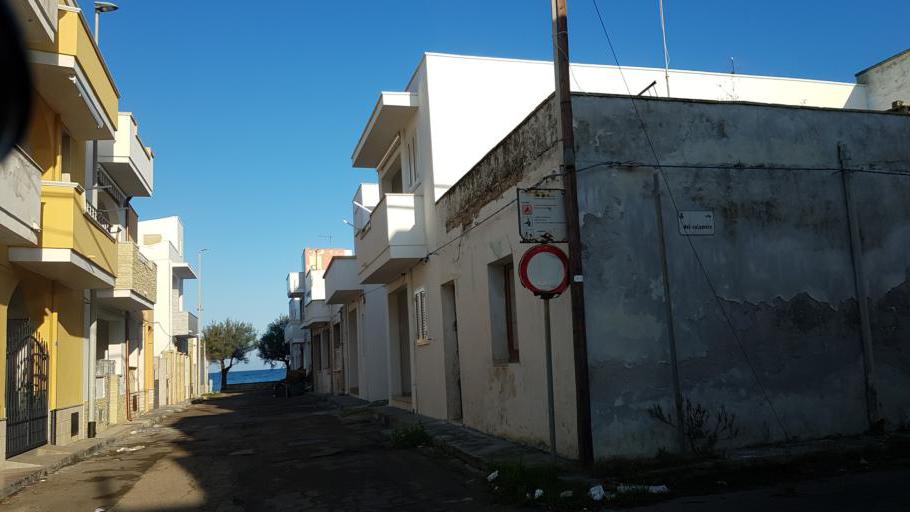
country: IT
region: Apulia
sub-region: Provincia di Brindisi
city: Torchiarolo
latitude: 40.5185
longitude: 18.0895
